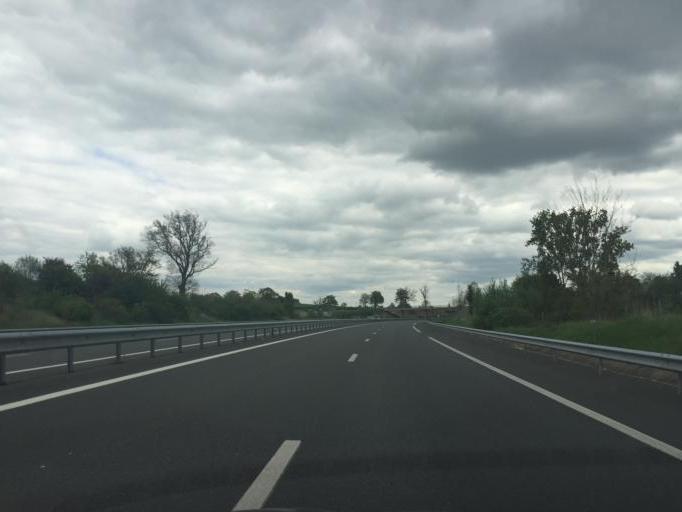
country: FR
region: Rhone-Alpes
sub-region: Departement de la Loire
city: La Pacaudiere
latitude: 46.1808
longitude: 3.8766
